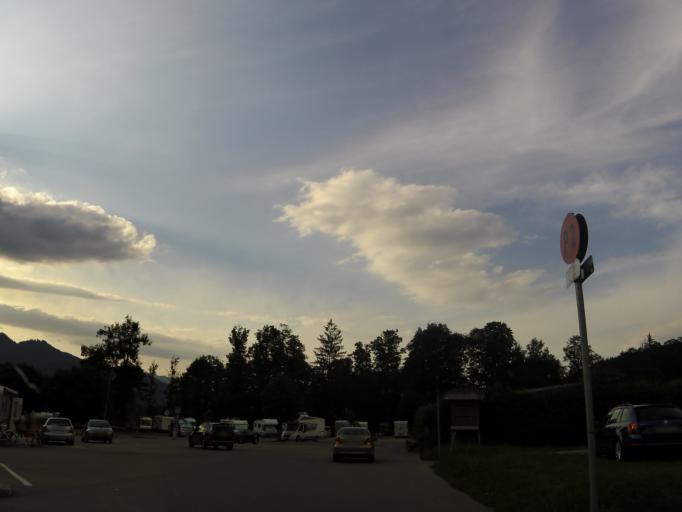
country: DE
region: Bavaria
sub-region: Upper Bavaria
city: Schoenau am Koenigssee
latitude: 47.5924
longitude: 12.9885
